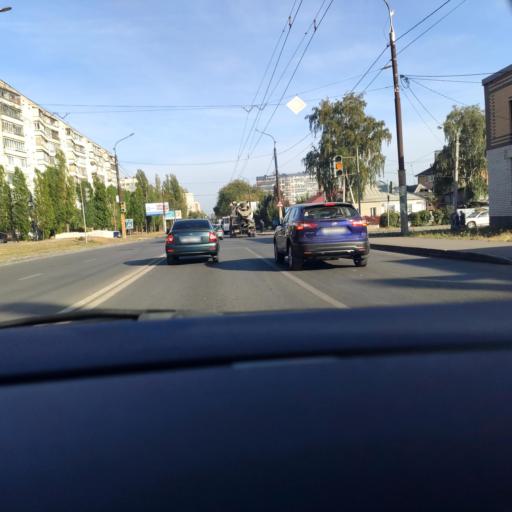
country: RU
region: Voronezj
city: Podgornoye
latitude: 51.7015
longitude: 39.1557
